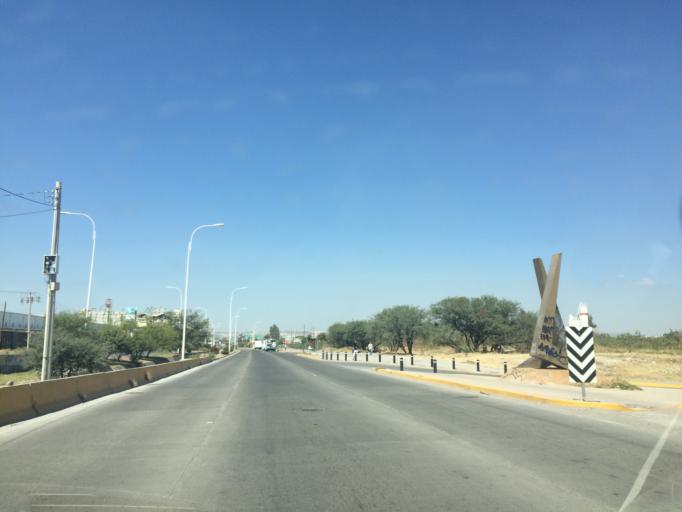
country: MX
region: Guanajuato
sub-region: Leon
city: San Jose de Duran (Los Troncoso)
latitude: 21.0826
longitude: -101.6627
